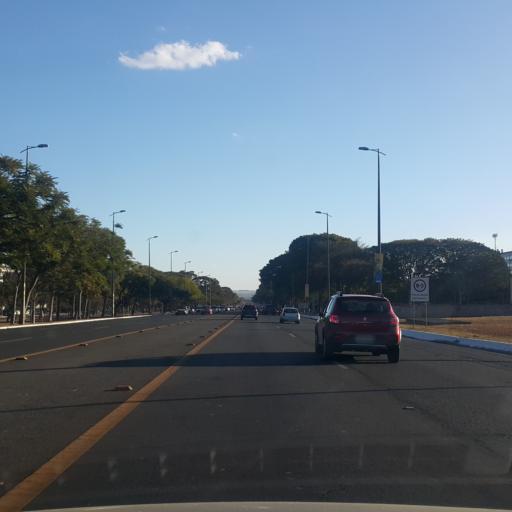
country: BR
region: Federal District
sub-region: Brasilia
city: Brasilia
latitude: -15.8225
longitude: -47.9085
